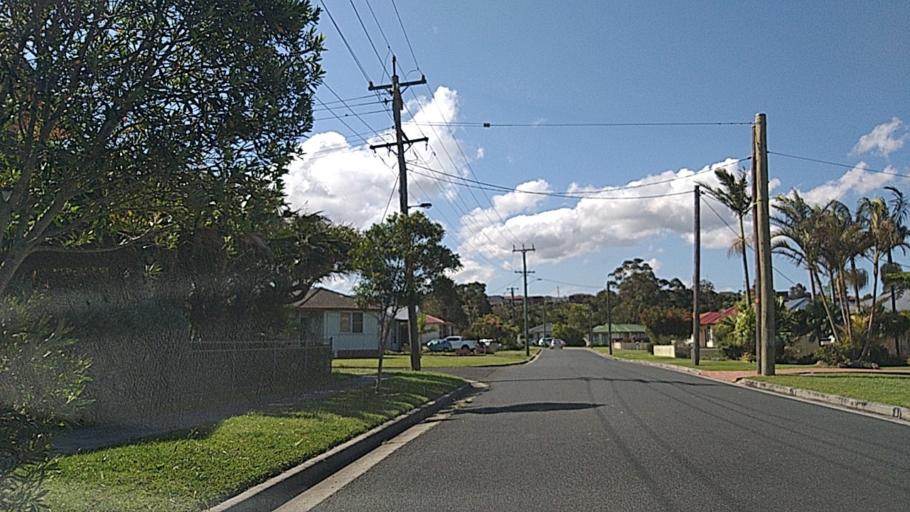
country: AU
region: New South Wales
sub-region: Wollongong
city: Cordeaux Heights
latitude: -34.4580
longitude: 150.8356
